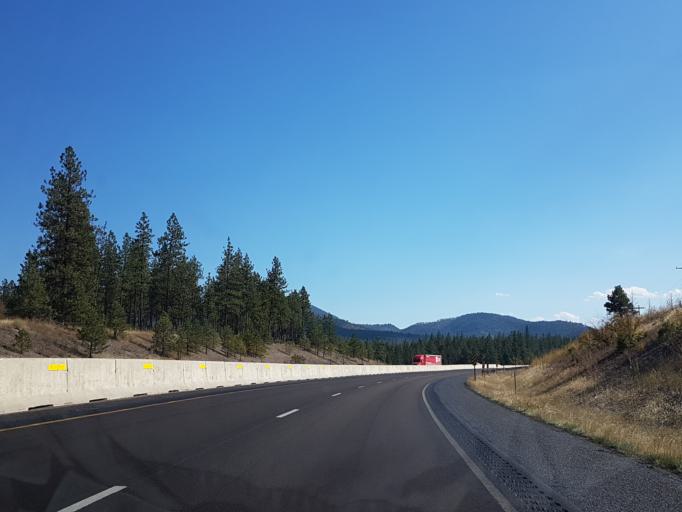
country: US
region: Montana
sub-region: Mineral County
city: Superior
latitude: 47.1339
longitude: -114.7990
